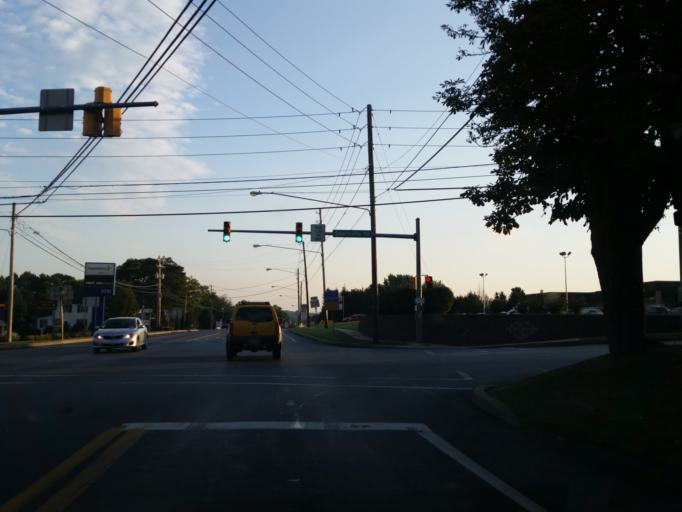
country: US
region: Pennsylvania
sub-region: Lancaster County
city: Swartzville
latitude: 40.2333
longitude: -76.0782
